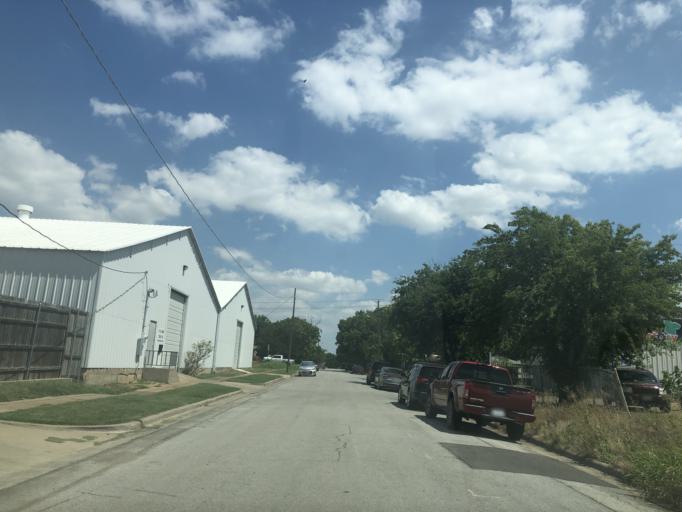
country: US
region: Texas
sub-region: Dallas County
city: Grand Prairie
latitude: 32.7419
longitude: -97.0241
